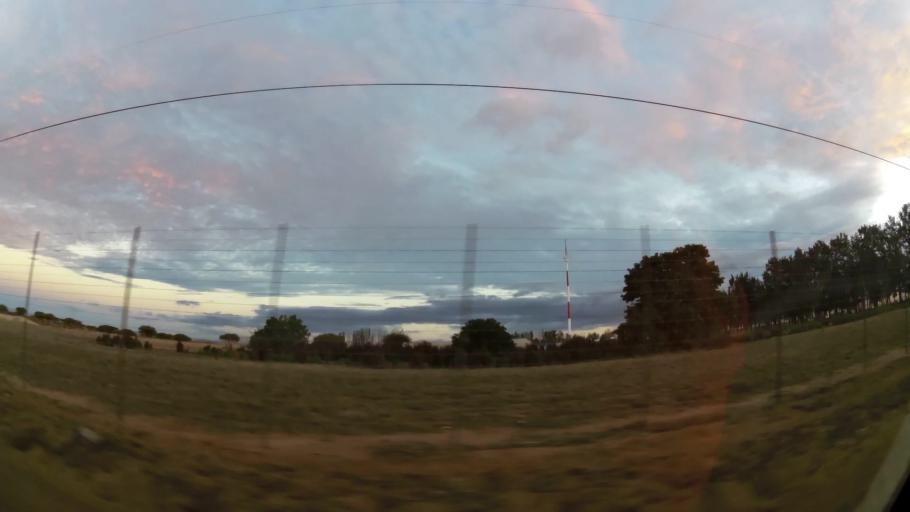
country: ZA
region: Limpopo
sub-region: Capricorn District Municipality
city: Polokwane
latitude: -23.7344
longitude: 29.4211
